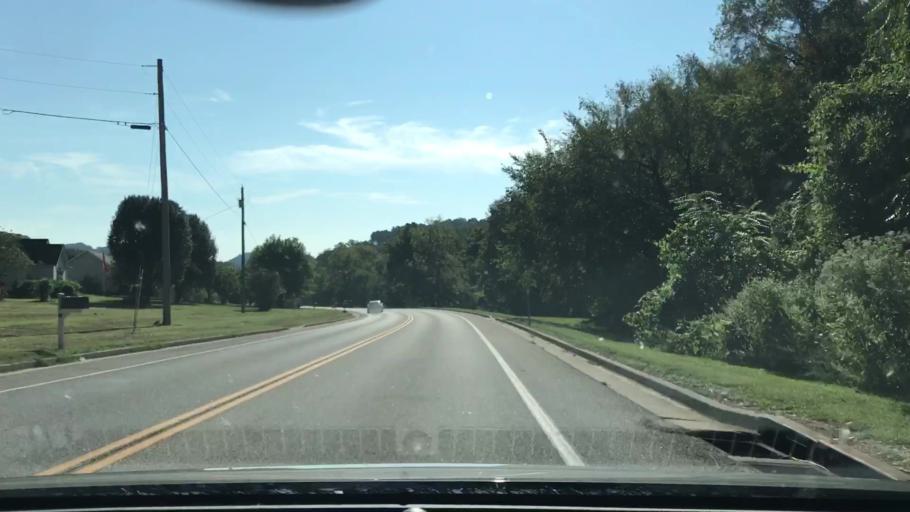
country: US
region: Tennessee
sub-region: Smith County
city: Carthage
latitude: 36.3203
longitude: -85.9205
